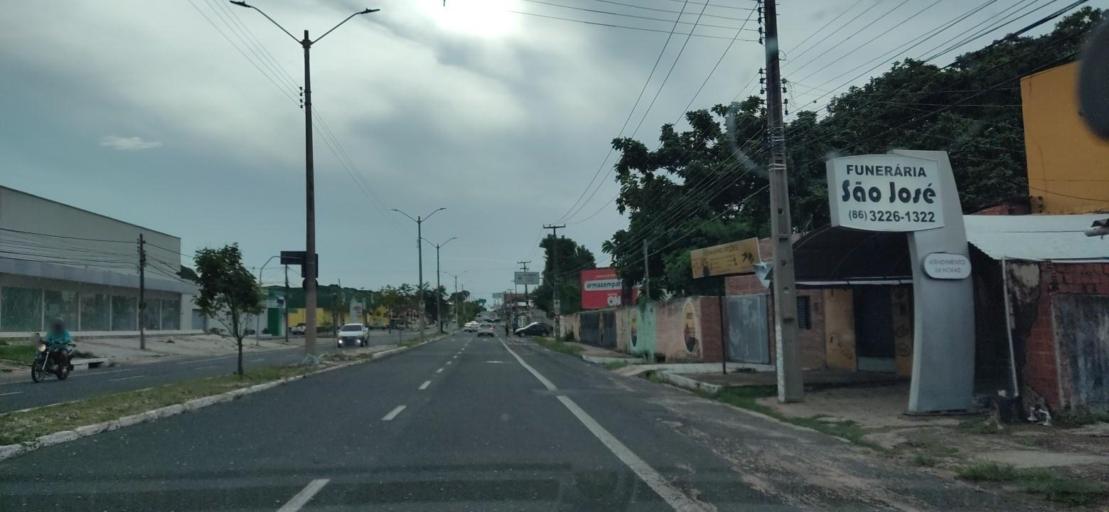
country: BR
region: Piaui
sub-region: Teresina
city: Teresina
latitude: -5.0952
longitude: -42.7907
